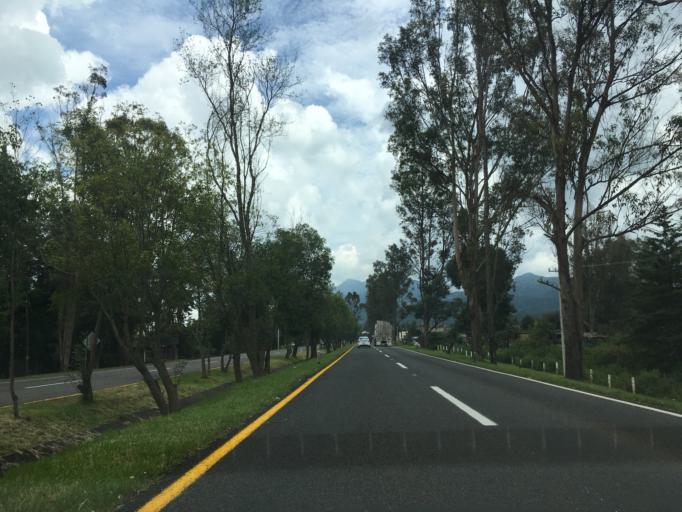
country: MX
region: Michoacan
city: Patzcuaro
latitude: 19.5432
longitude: -101.5843
